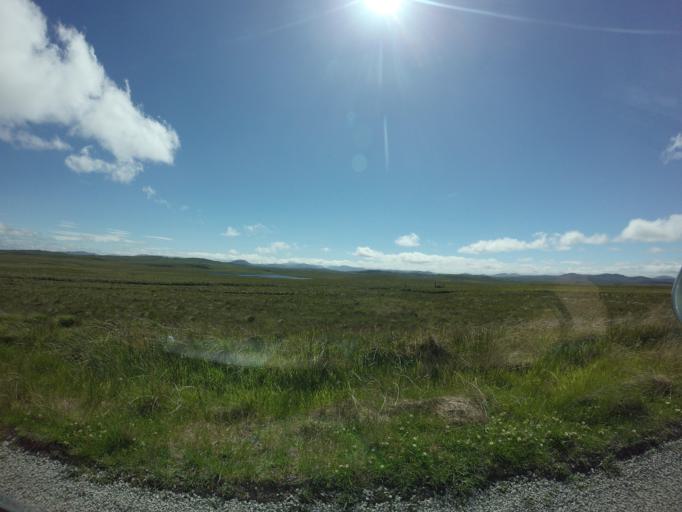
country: GB
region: Scotland
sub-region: Eilean Siar
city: Isle of Lewis
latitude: 58.1844
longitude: -6.6741
